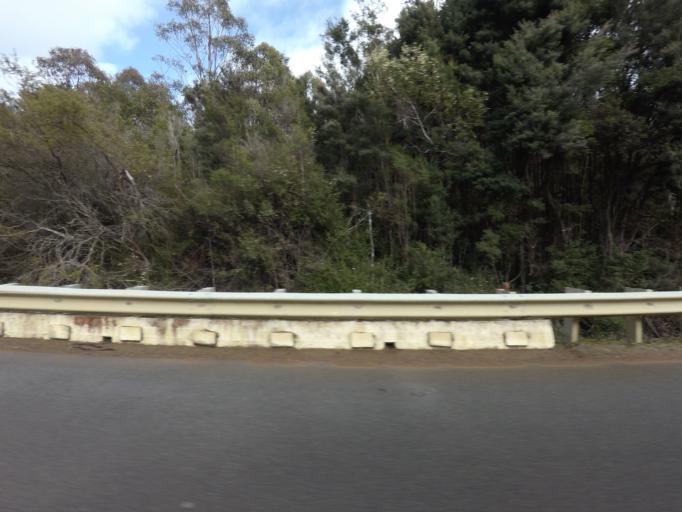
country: AU
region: Tasmania
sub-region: Huon Valley
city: Geeveston
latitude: -43.3656
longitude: 146.9589
